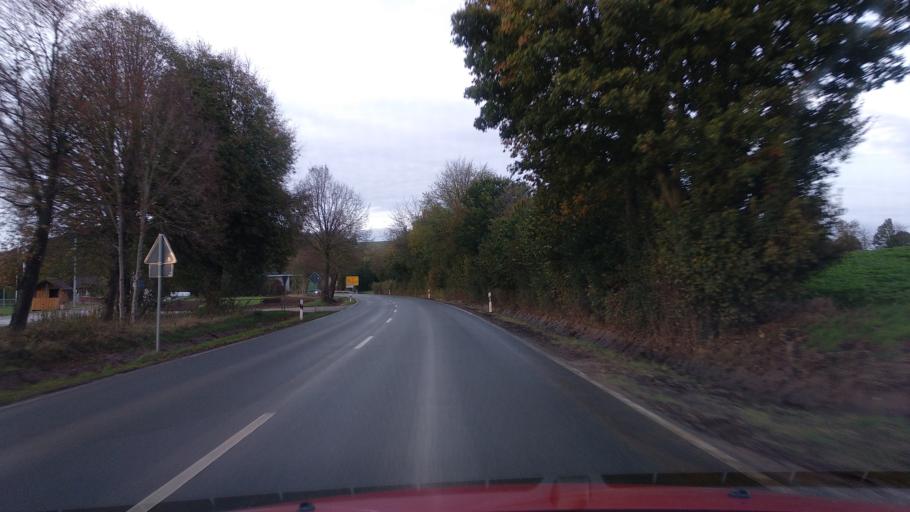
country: DE
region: North Rhine-Westphalia
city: Brakel
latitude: 51.6976
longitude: 9.2163
